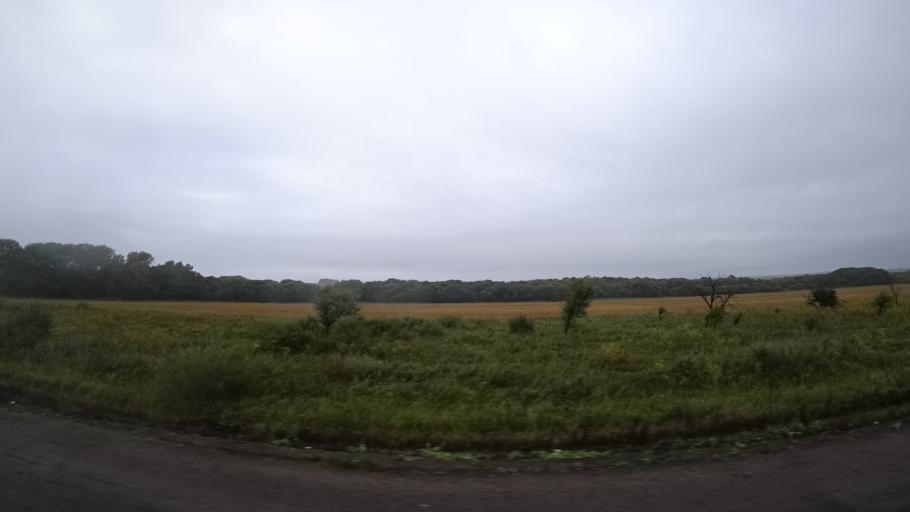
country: RU
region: Primorskiy
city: Monastyrishche
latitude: 44.2787
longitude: 132.4894
